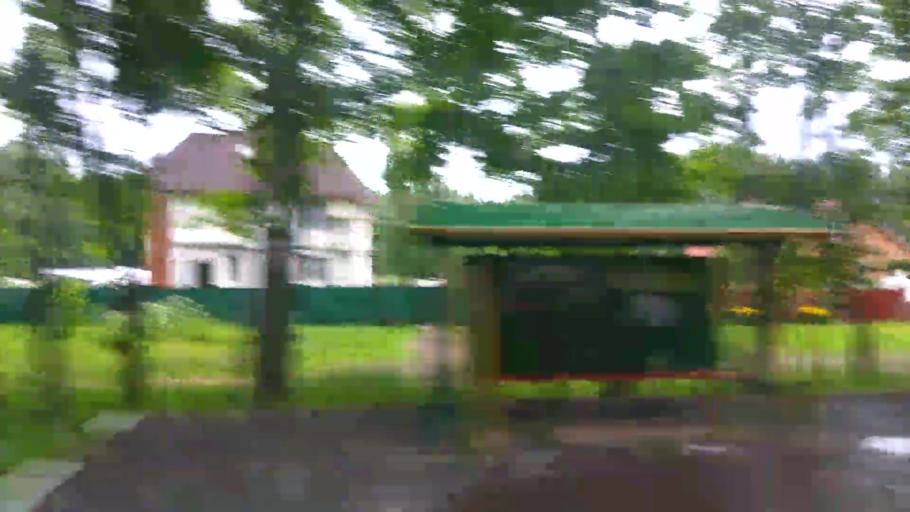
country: RU
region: Moskovskaya
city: Ozherel'ye
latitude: 54.8349
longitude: 38.2784
